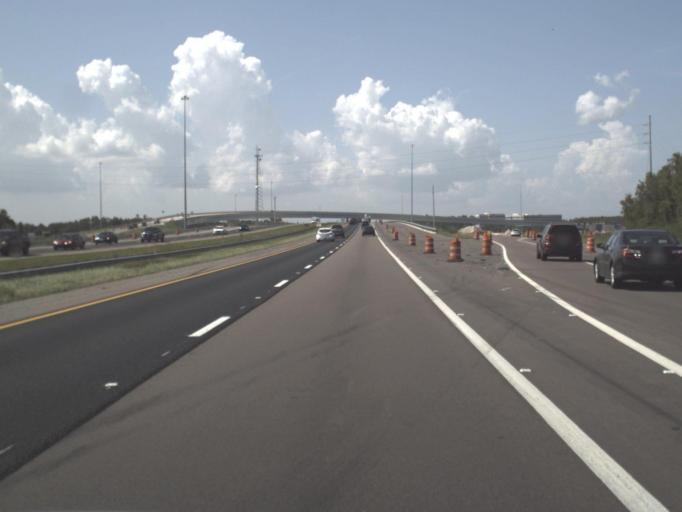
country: US
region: Florida
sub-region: Hillsborough County
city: Pebble Creek
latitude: 28.1163
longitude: -82.3721
